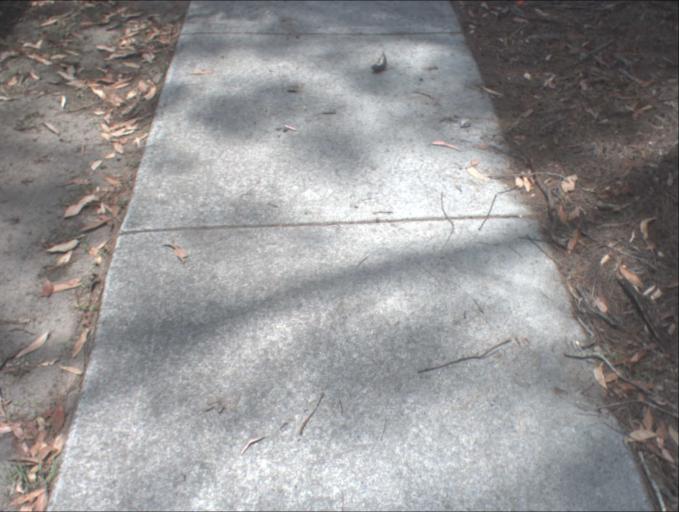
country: AU
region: Queensland
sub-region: Logan
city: Windaroo
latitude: -27.7430
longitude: 153.1884
